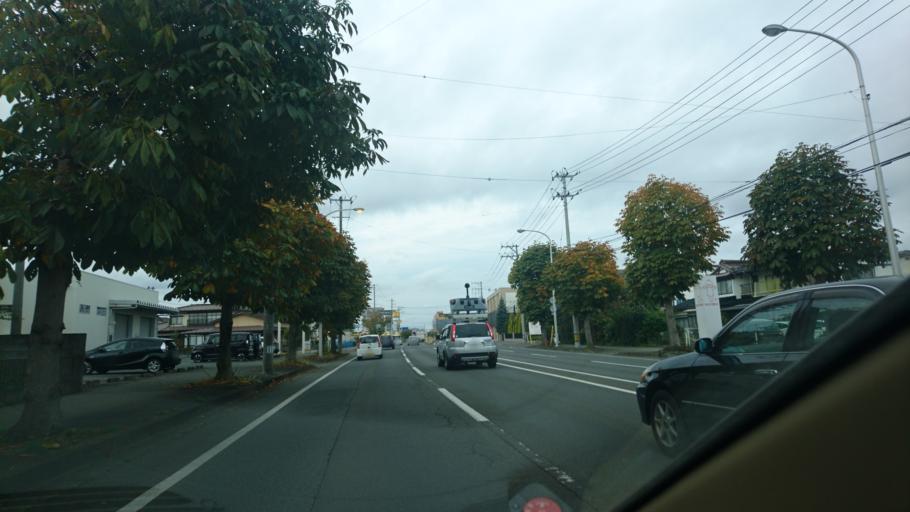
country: JP
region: Iwate
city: Morioka-shi
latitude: 39.6845
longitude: 141.1413
